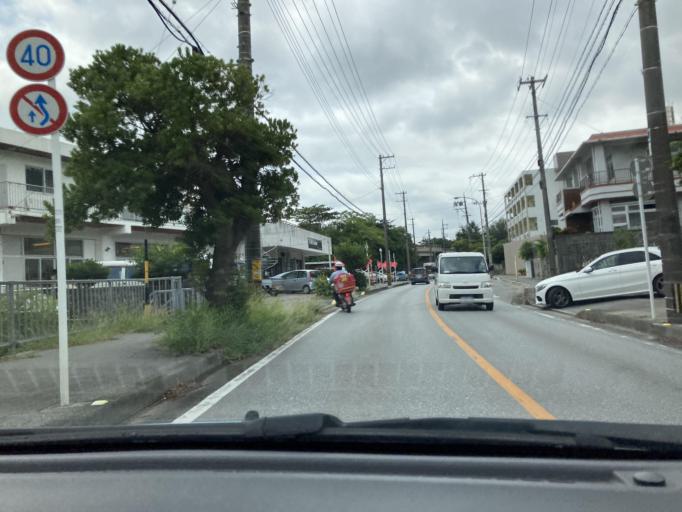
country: JP
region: Okinawa
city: Ginowan
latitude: 26.2815
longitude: 127.7848
